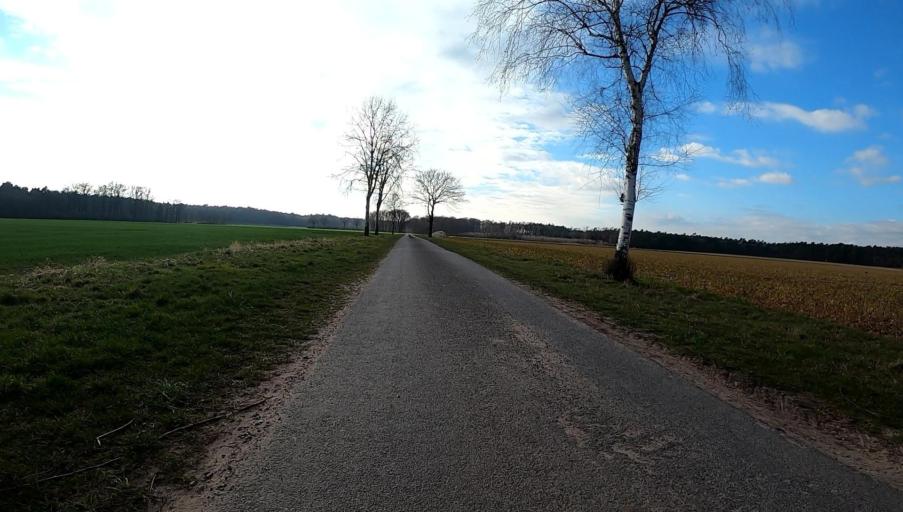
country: DE
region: Lower Saxony
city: Schwarmstedt
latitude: 52.6184
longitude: 9.6267
